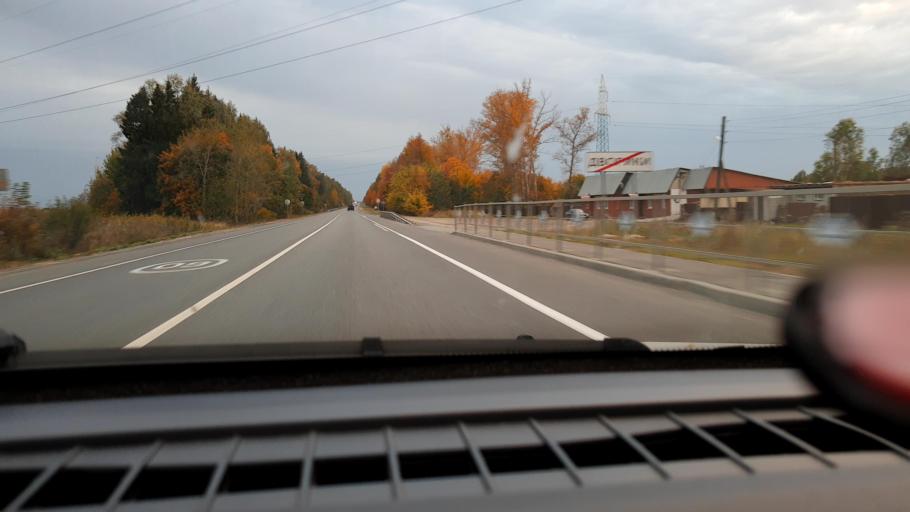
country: RU
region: Vladimir
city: Orgtrud
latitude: 56.1988
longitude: 40.8362
